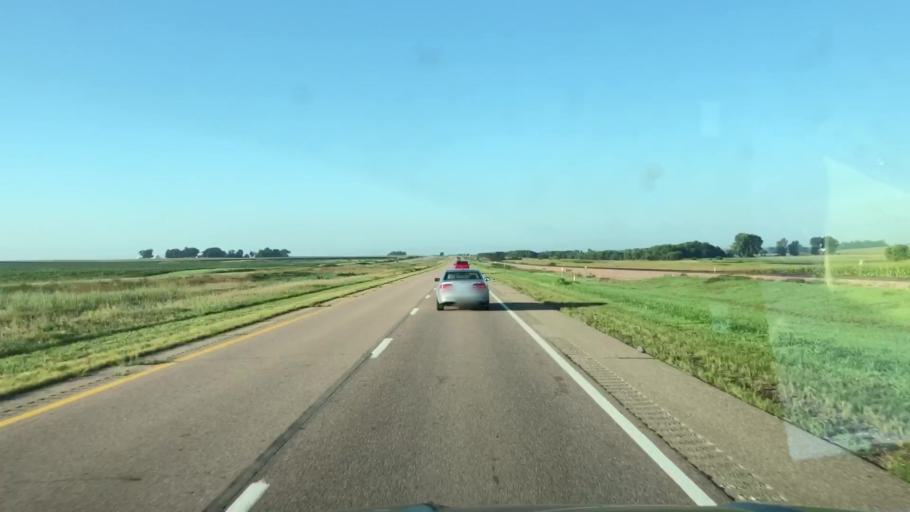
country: US
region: Iowa
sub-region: O'Brien County
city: Sheldon
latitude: 43.1260
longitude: -95.8861
